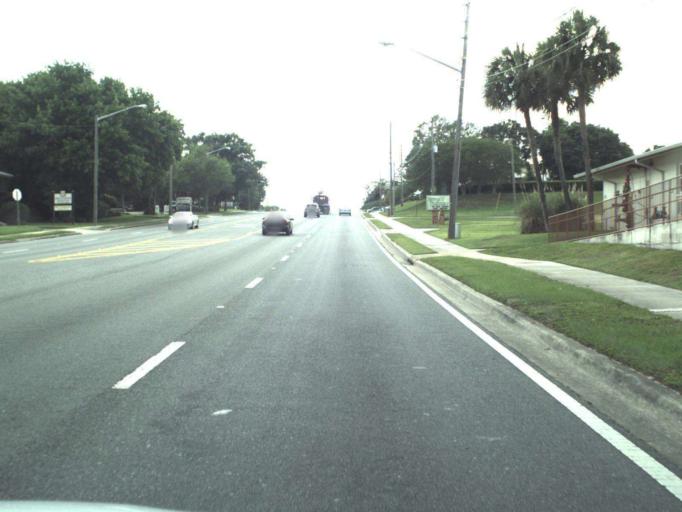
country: US
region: Florida
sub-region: Marion County
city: Ocala
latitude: 29.1717
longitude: -82.1301
